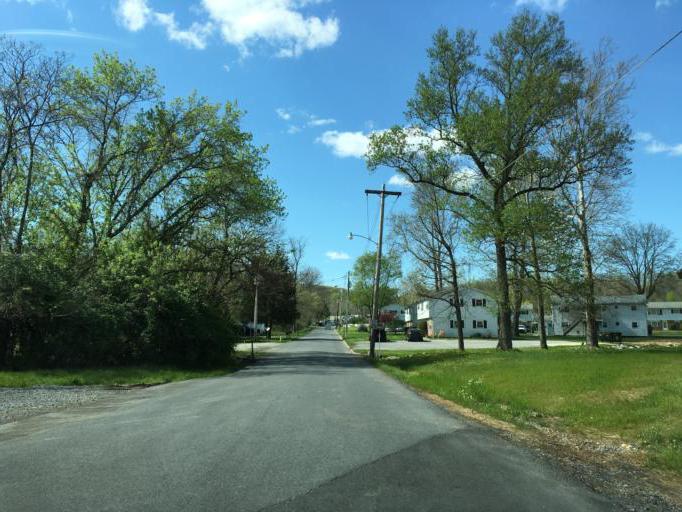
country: US
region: Maryland
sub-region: Frederick County
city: Thurmont
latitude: 39.6170
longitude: -77.4086
